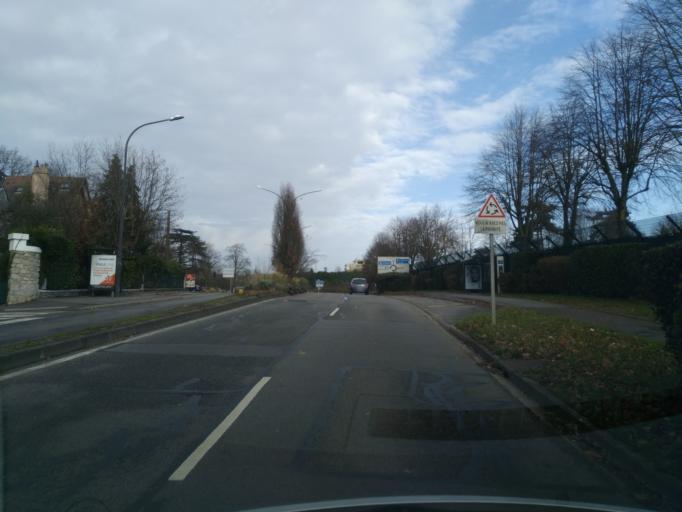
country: FR
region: Ile-de-France
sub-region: Departement des Yvelines
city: Le Chesnay
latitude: 48.8338
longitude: 2.1291
